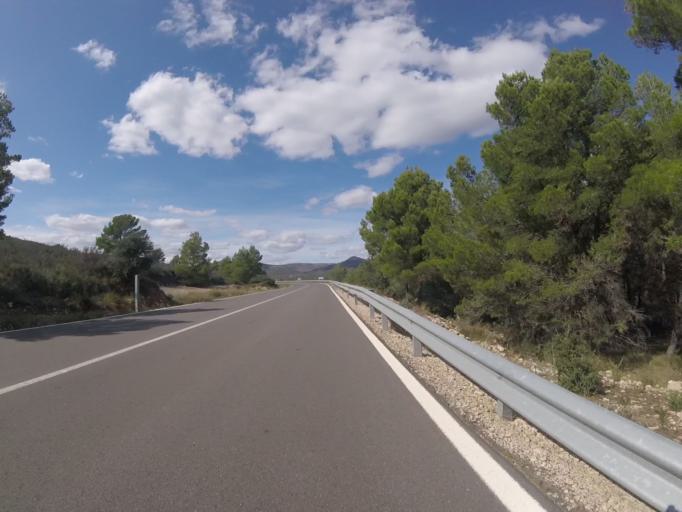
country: ES
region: Valencia
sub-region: Provincia de Castello
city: Chert/Xert
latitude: 40.4400
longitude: 0.1106
